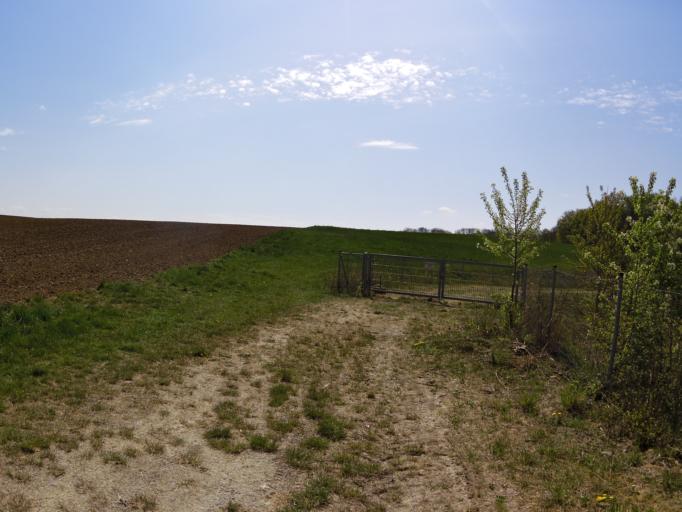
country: DE
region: Bavaria
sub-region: Regierungsbezirk Unterfranken
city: Giebelstadt
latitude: 49.6949
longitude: 9.9508
